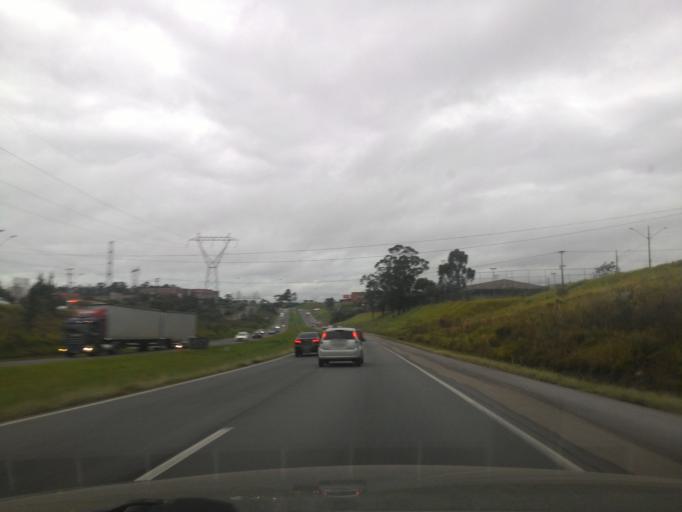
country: BR
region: Parana
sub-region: Araucaria
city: Araucaria
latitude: -25.5461
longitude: -49.3174
